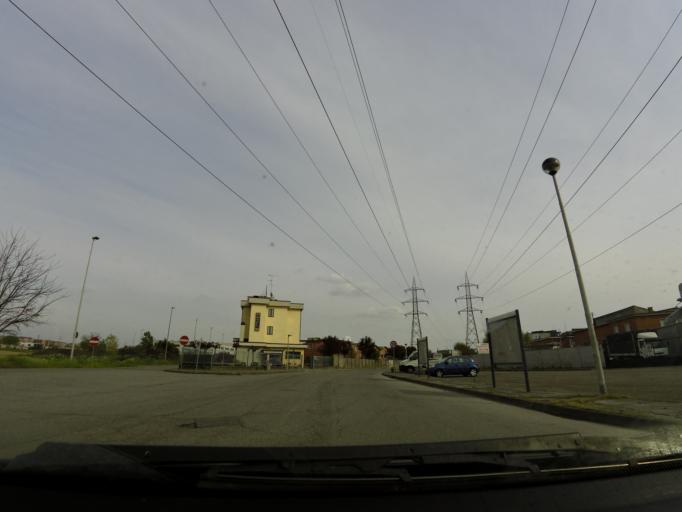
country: IT
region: Lombardy
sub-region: Citta metropolitana di Milano
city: Chiaravalle
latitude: 45.4032
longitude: 9.2484
